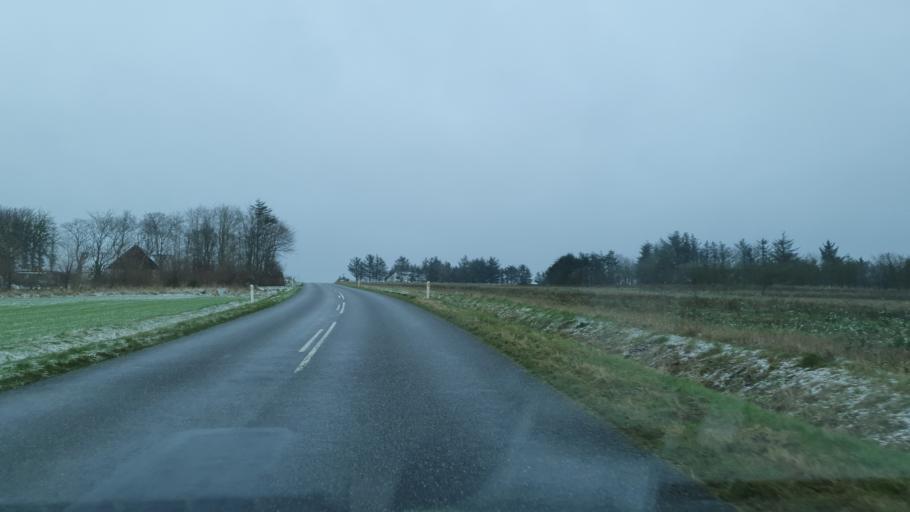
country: DK
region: North Denmark
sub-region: Jammerbugt Kommune
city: Brovst
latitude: 57.1265
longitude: 9.4779
